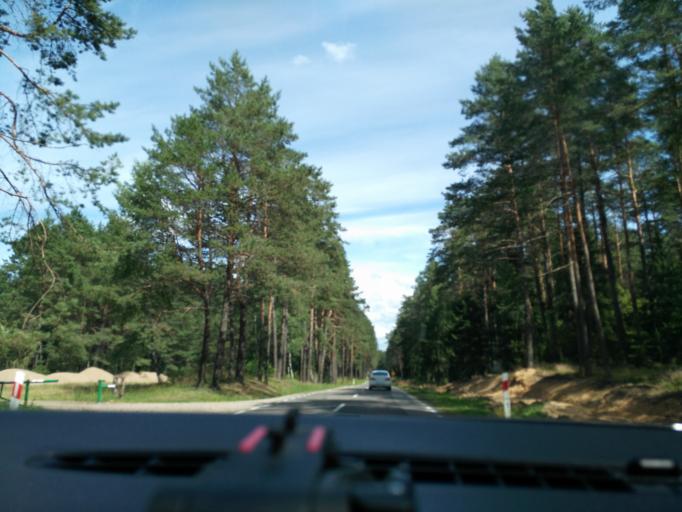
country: PL
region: Podlasie
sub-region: Powiat augustowski
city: Augustow
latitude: 53.8548
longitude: 23.0644
